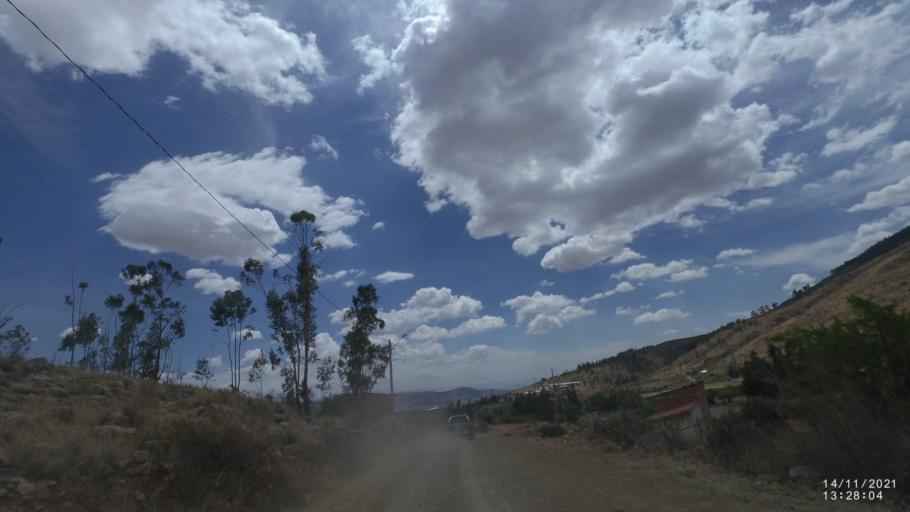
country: BO
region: Cochabamba
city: Colomi
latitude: -17.3849
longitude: -65.9831
